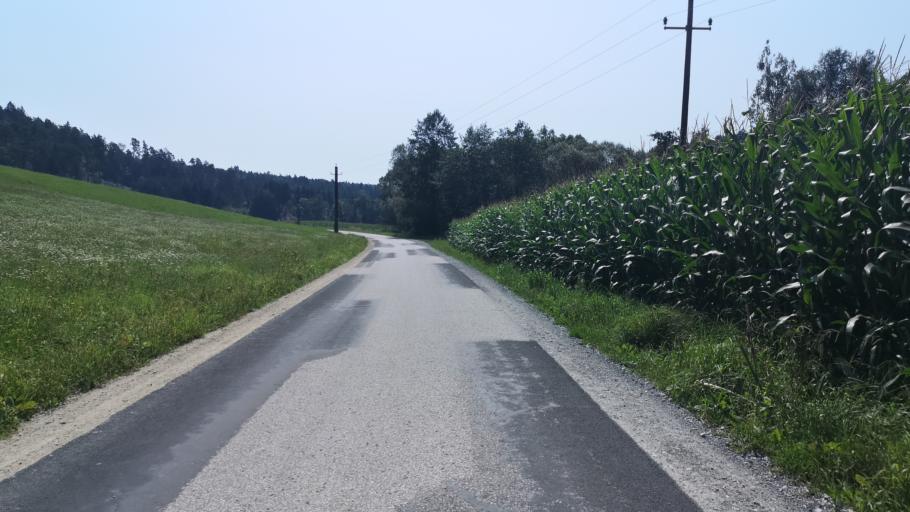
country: AT
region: Styria
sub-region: Politischer Bezirk Deutschlandsberg
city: Sankt Josef (Weststeiermark)
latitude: 46.8906
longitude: 15.3671
